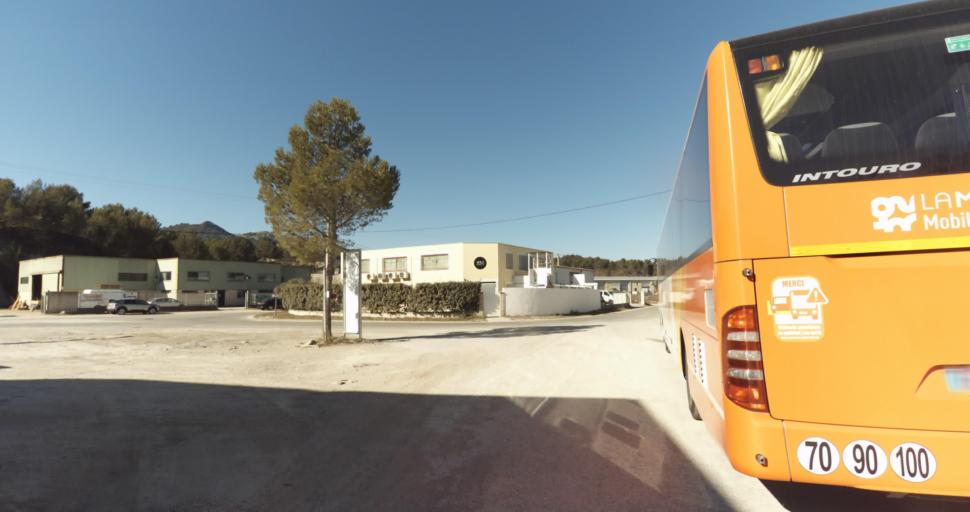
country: FR
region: Provence-Alpes-Cote d'Azur
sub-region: Departement des Bouches-du-Rhone
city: Cadolive
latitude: 43.3973
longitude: 5.5635
